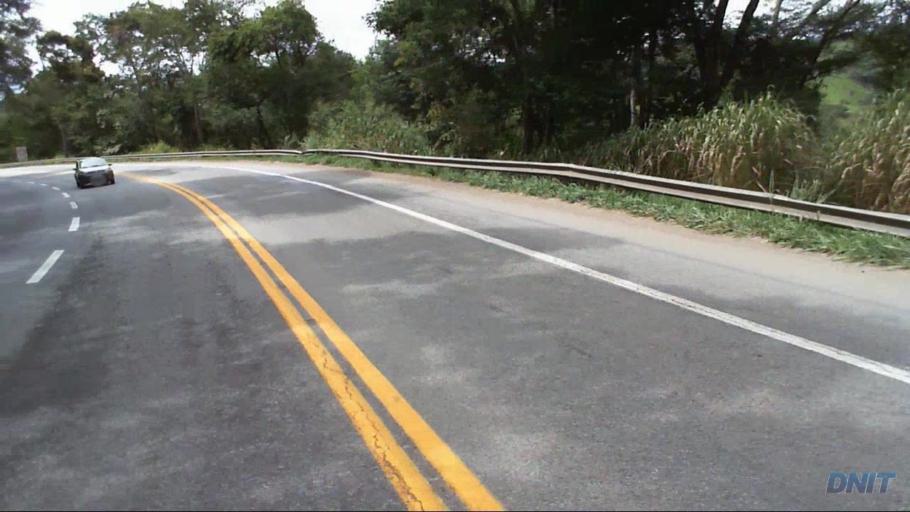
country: BR
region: Minas Gerais
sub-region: Caete
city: Caete
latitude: -19.7539
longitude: -43.6304
